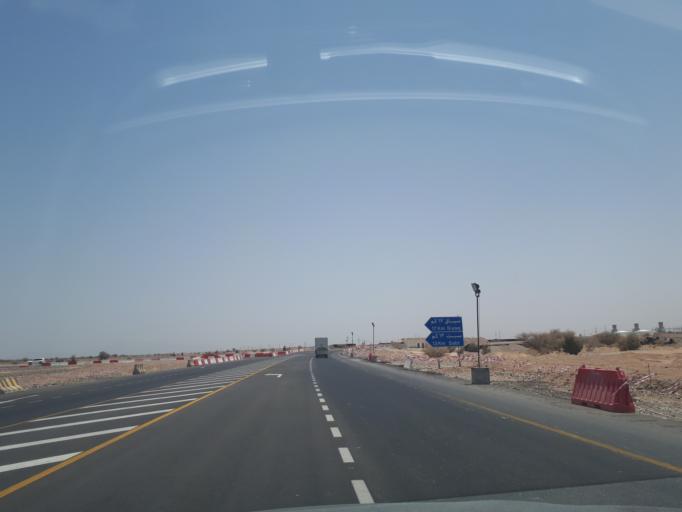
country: OM
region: Ash Sharqiyah
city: Badiyah
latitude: 22.4009
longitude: 59.0689
